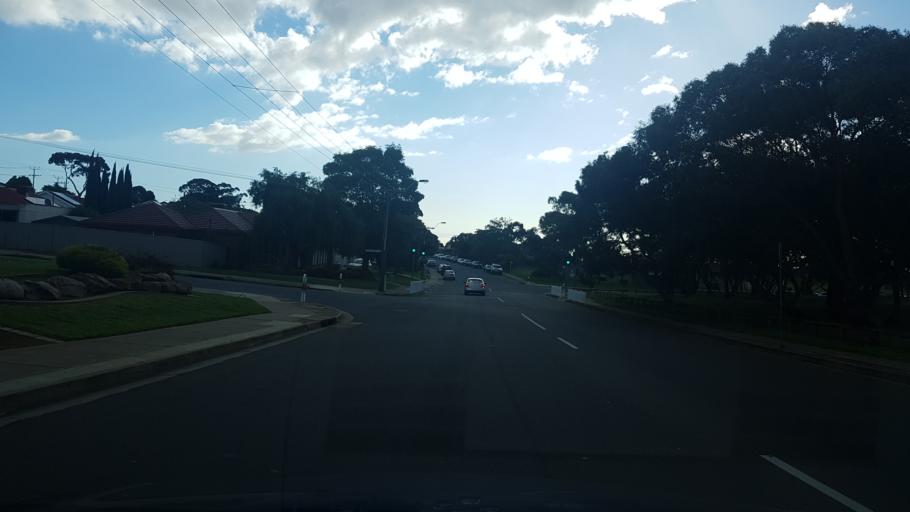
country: AU
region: South Australia
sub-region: Salisbury
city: Ingle Farm
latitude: -34.8298
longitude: 138.6411
